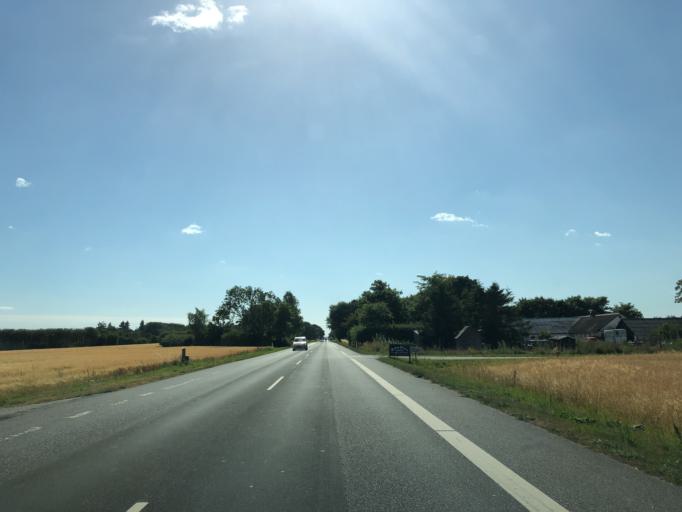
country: DK
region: North Denmark
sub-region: Mariagerfjord Kommune
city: Hobro
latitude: 56.6291
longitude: 9.7512
